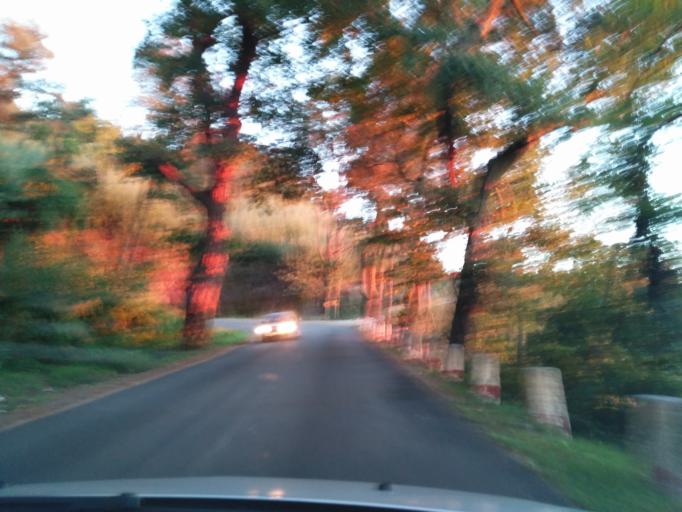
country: PT
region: Braga
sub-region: Braga
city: Adaufe
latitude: 41.5521
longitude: -8.3798
